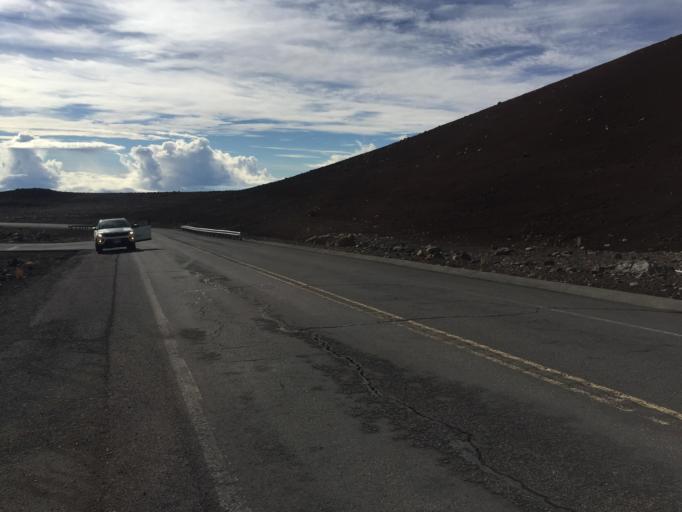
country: US
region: Hawaii
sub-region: Hawaii County
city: Honoka'a
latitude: 19.7937
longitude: -155.4590
